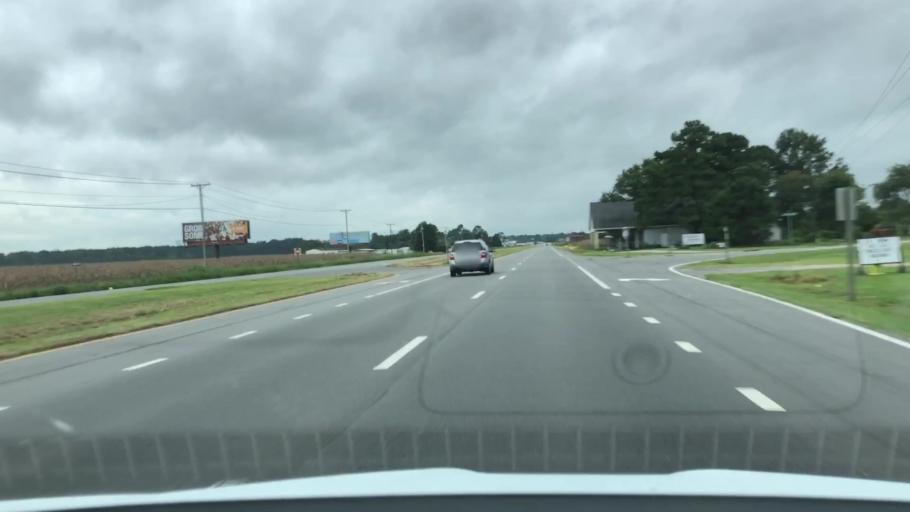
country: US
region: North Carolina
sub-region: Lenoir County
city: La Grange
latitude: 35.2641
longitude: -77.7234
